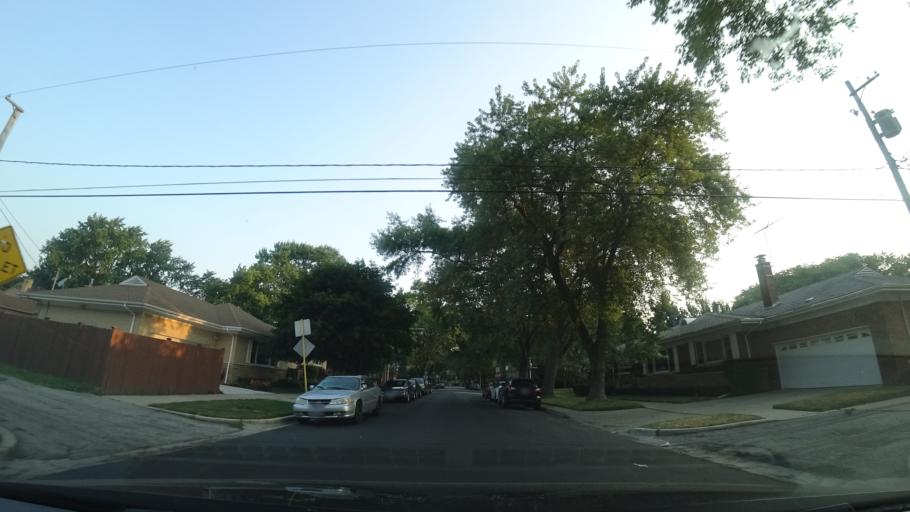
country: US
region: Illinois
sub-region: Cook County
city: Lincolnwood
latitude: 41.9788
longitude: -87.7015
